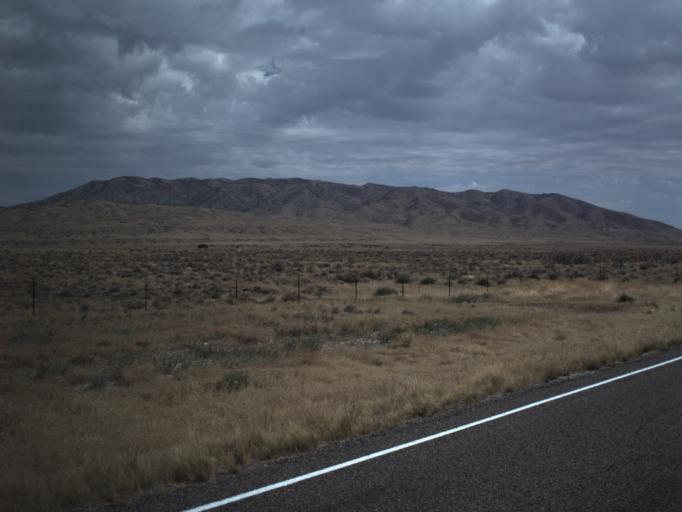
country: US
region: Utah
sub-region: Tooele County
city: Wendover
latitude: 41.4350
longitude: -113.7609
